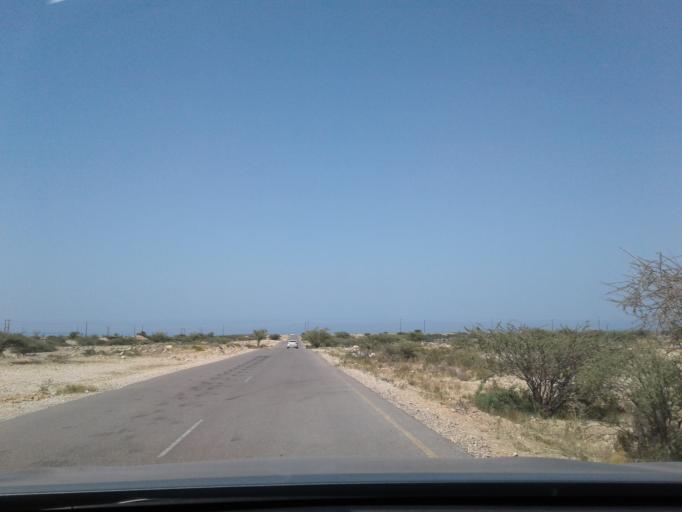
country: OM
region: Ash Sharqiyah
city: Al Qabil
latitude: 23.0374
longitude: 59.0704
